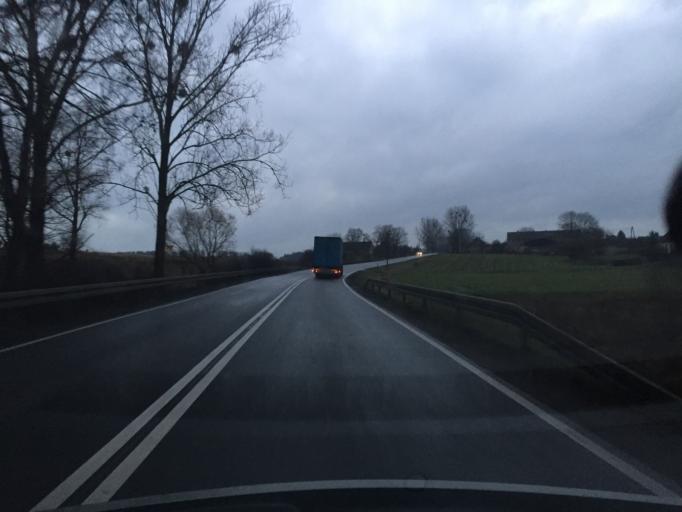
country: PL
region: Kujawsko-Pomorskie
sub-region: Powiat brodnicki
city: Bobrowo
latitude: 53.2489
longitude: 19.3049
